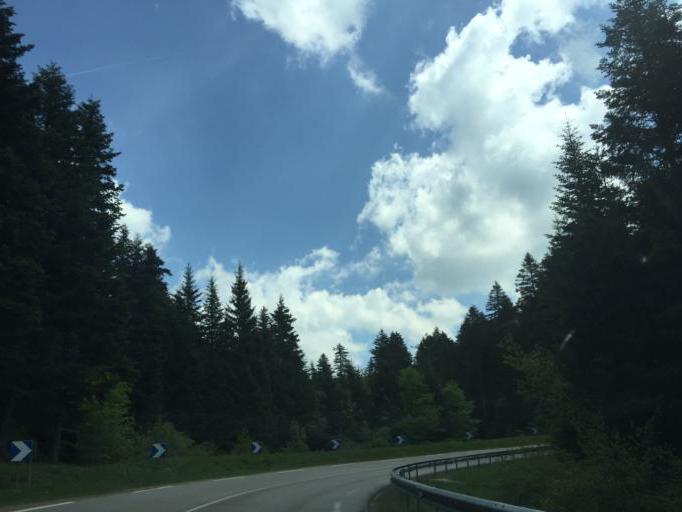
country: FR
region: Rhone-Alpes
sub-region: Departement de la Loire
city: Saint-Genest-Malifaux
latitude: 45.3456
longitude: 4.4828
